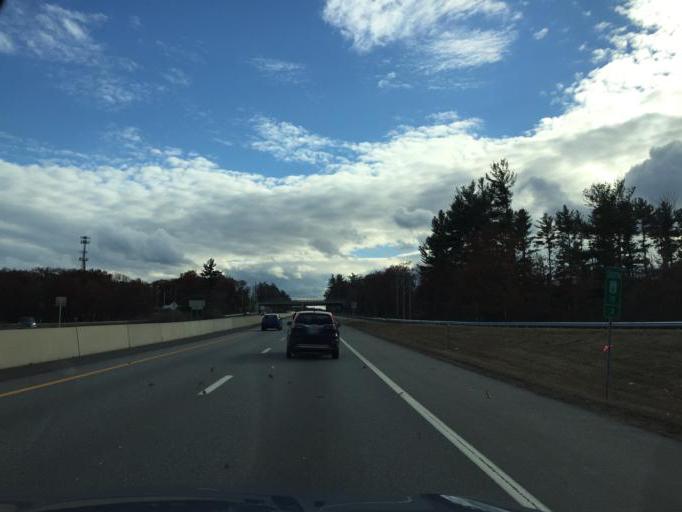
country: US
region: New Hampshire
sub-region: Hillsborough County
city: Bedford
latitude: 42.9467
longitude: -71.4716
